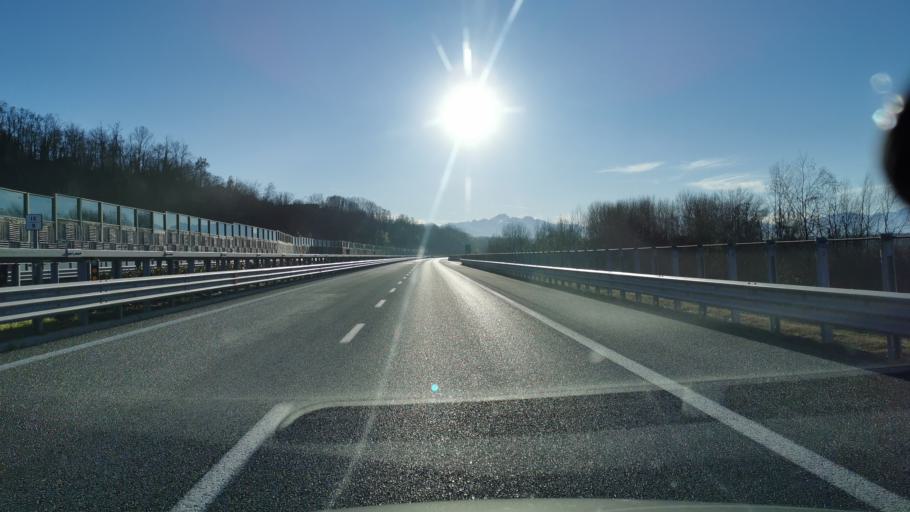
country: IT
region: Piedmont
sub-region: Provincia di Cuneo
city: Montanera
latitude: 44.4642
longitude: 7.6638
